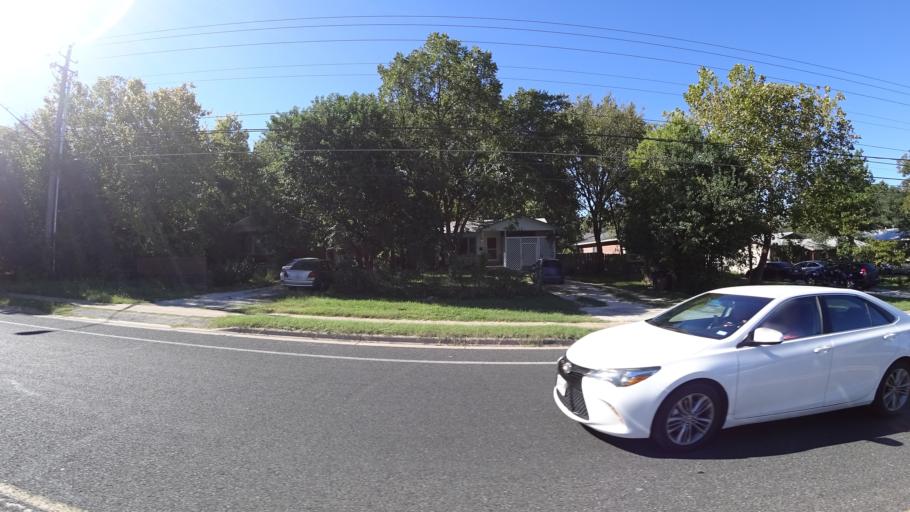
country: US
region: Texas
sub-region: Travis County
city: Austin
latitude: 30.2284
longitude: -97.7575
